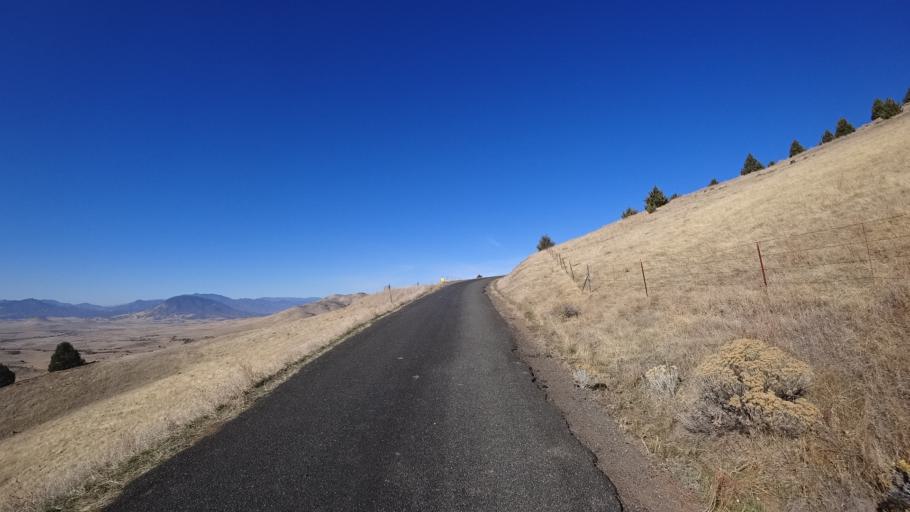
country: US
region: California
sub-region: Siskiyou County
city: Montague
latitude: 41.8247
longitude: -122.3373
